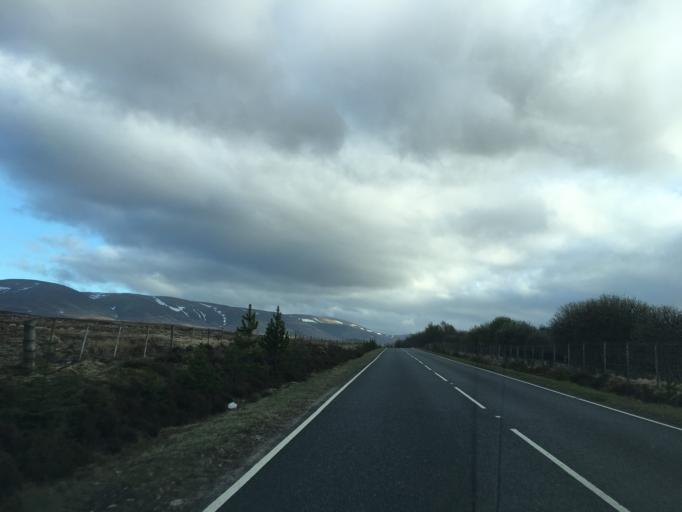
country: GB
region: Scotland
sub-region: Highland
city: Kingussie
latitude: 56.9514
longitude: -4.2442
